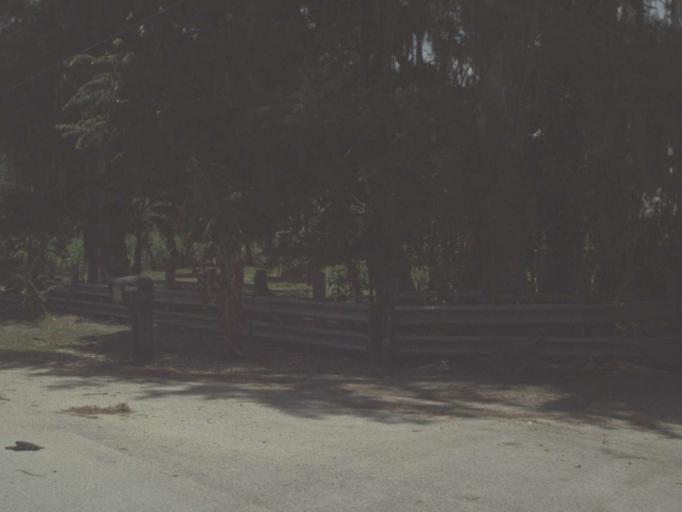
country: US
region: Florida
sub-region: Martin County
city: Indiantown
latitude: 27.0235
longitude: -80.6314
